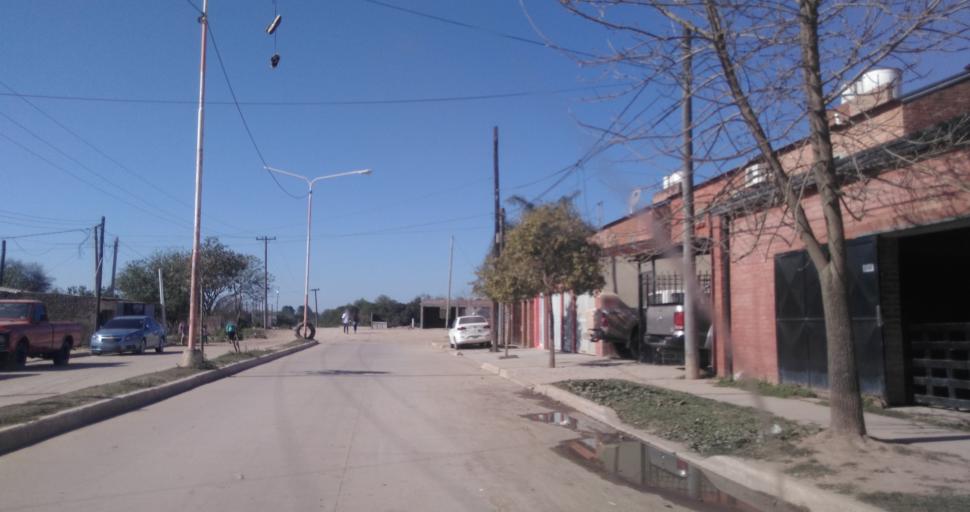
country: AR
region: Chaco
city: Resistencia
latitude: -27.4509
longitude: -58.9649
